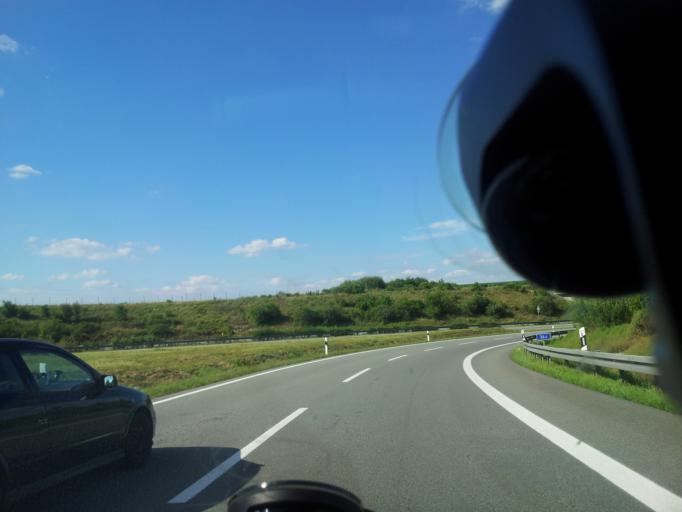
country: DE
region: Lower Saxony
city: Vienenburg
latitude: 51.9375
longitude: 10.5880
